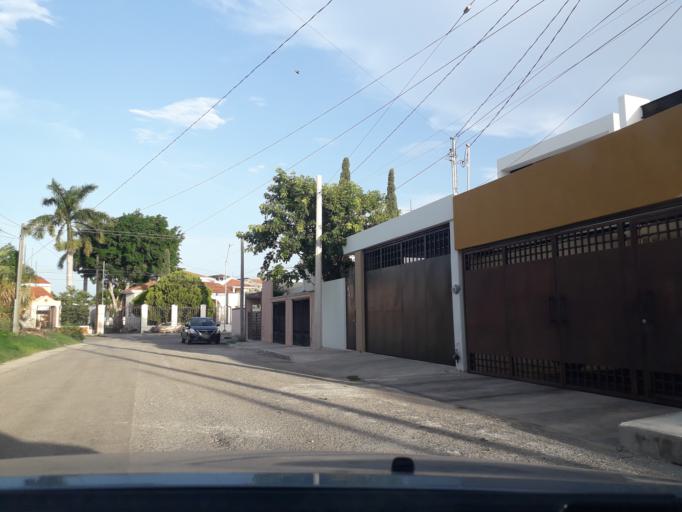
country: MX
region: Yucatan
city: Merida
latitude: 21.0058
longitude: -89.6400
